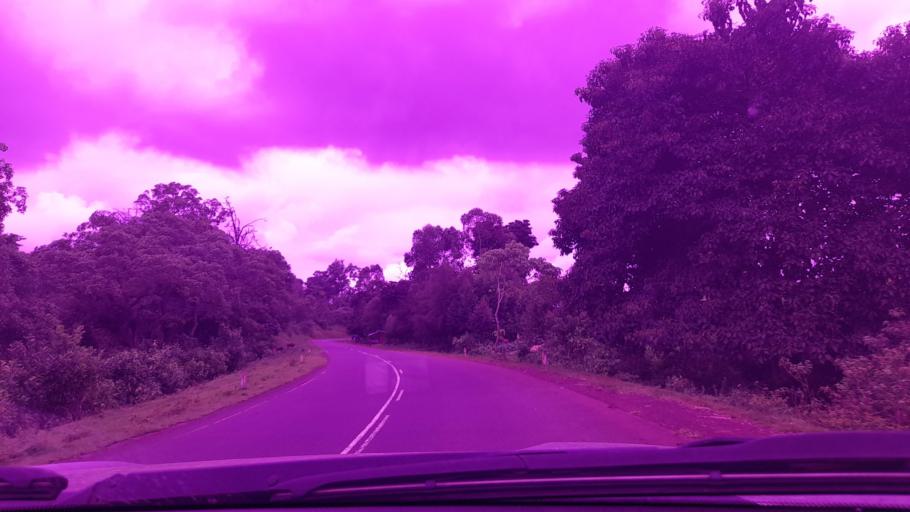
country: ET
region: Southern Nations, Nationalities, and People's Region
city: Bonga
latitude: 7.2822
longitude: 35.9555
